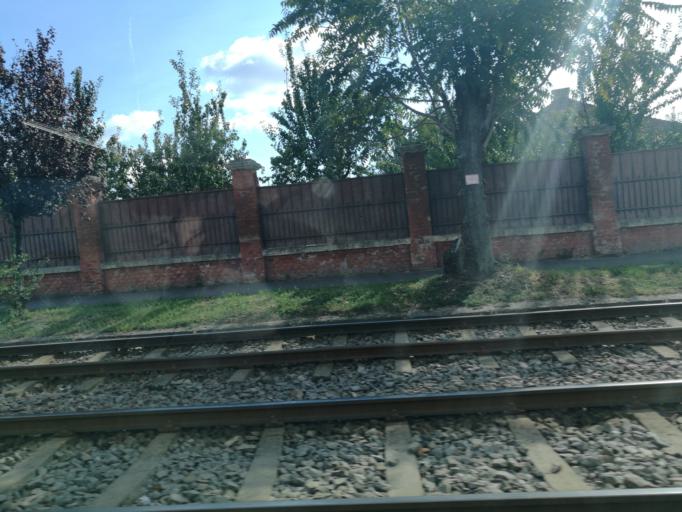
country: RO
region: Bihor
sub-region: Comuna Biharea
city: Oradea
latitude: 47.0550
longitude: 21.9149
